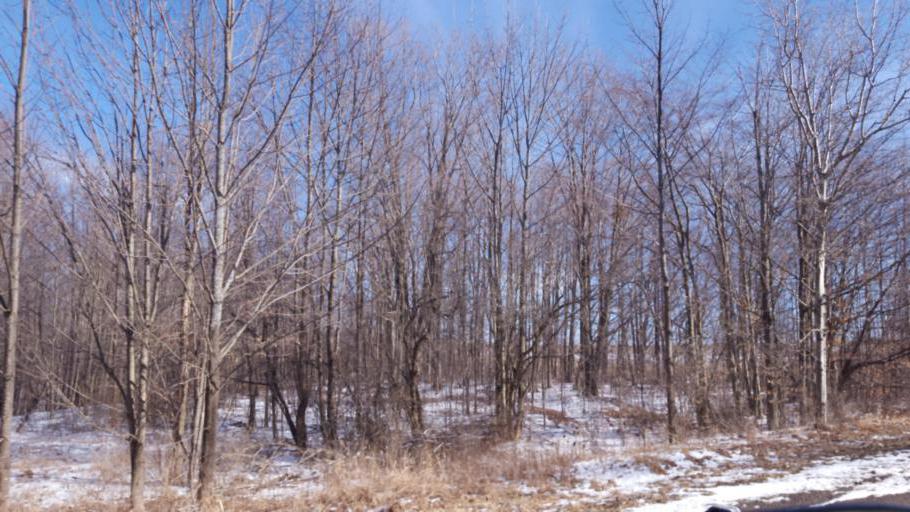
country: US
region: New York
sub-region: Allegany County
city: Wellsville
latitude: 42.1122
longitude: -77.9953
